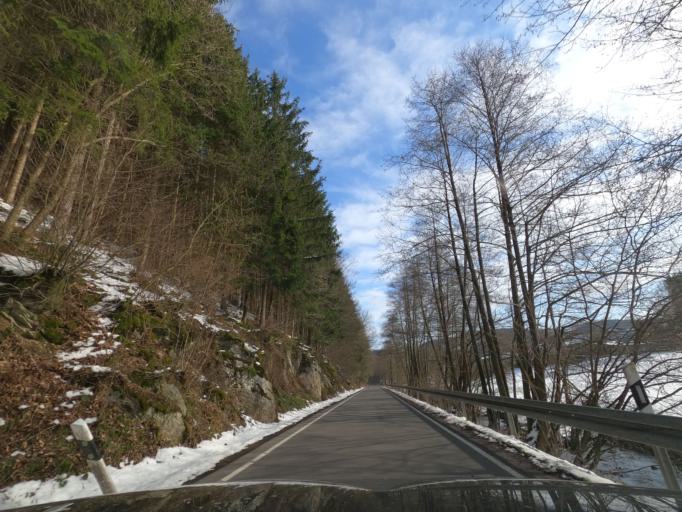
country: DE
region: North Rhine-Westphalia
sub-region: Regierungsbezirk Arnsberg
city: Herscheid
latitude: 51.1182
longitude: 7.8007
